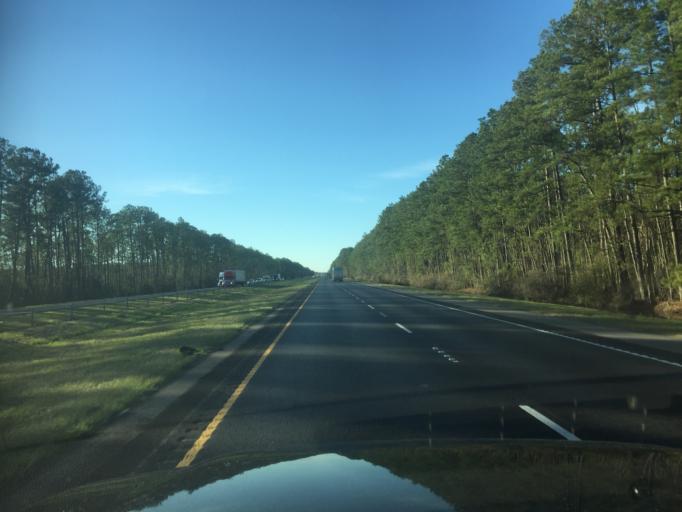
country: US
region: Louisiana
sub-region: Saint Tammany Parish
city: Lacombe
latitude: 30.3800
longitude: -89.9742
